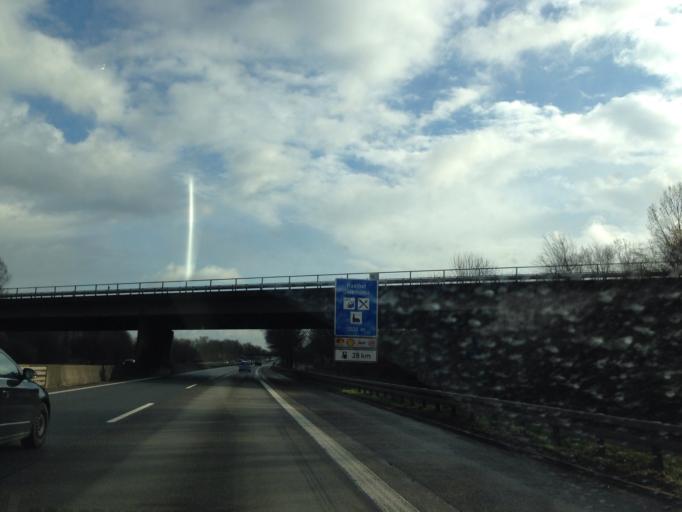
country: DE
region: North Rhine-Westphalia
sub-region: Regierungsbezirk Dusseldorf
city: Krefeld
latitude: 51.3262
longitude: 6.6299
